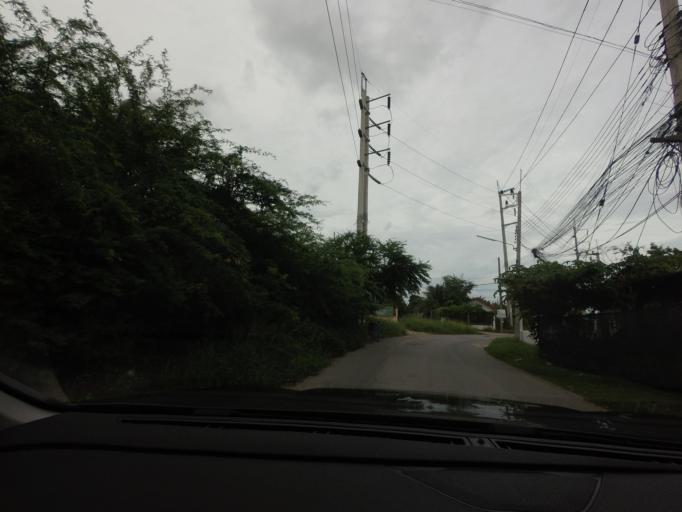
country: TH
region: Prachuap Khiri Khan
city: Hua Hin
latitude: 12.5381
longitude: 99.9509
